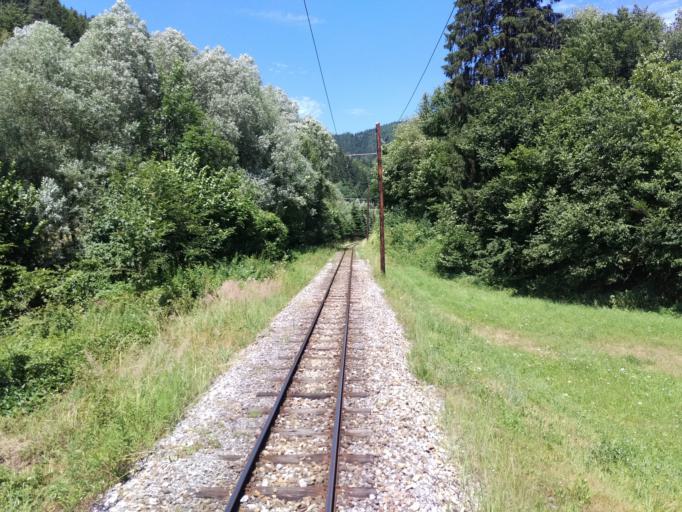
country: AT
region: Styria
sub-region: Politischer Bezirk Bruck-Muerzzuschlag
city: Pernegg an der Mur
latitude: 47.3561
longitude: 15.3684
